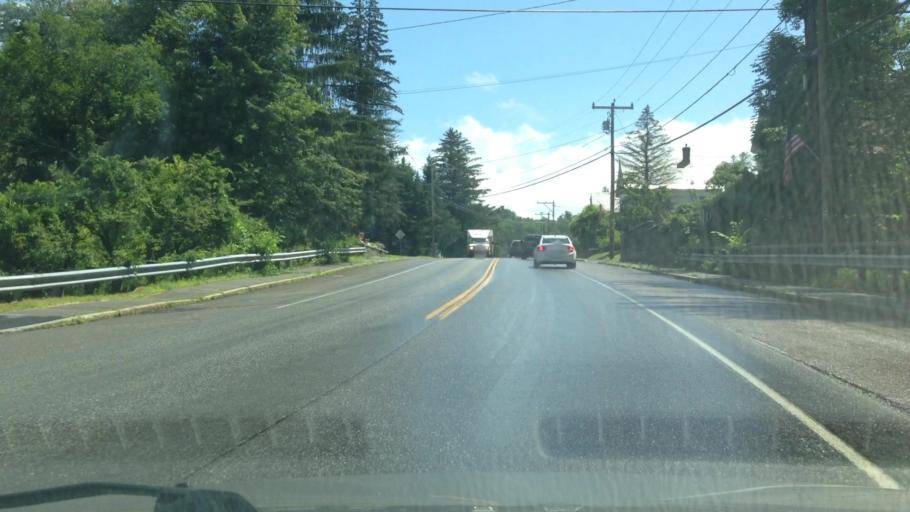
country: US
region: New Hampshire
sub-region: Cheshire County
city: Marlborough
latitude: 42.9082
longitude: -72.2164
